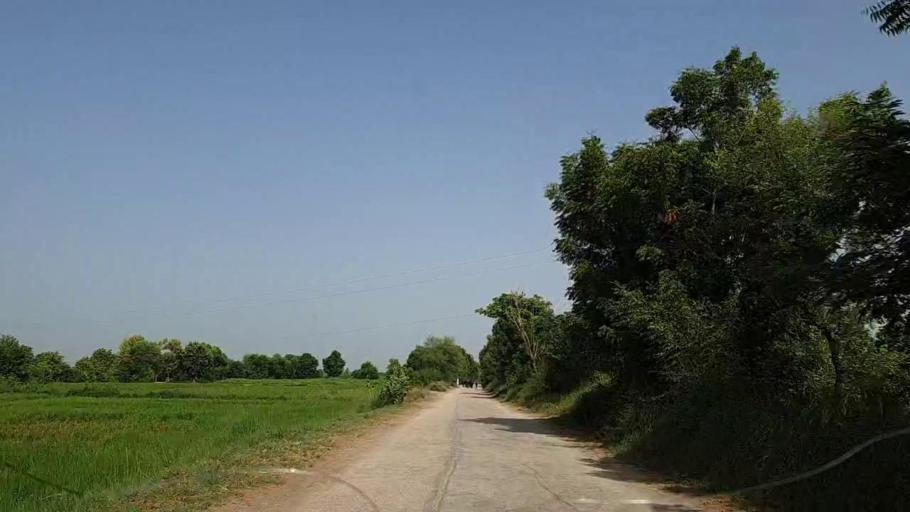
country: PK
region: Sindh
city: Kandiaro
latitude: 27.0690
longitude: 68.1670
